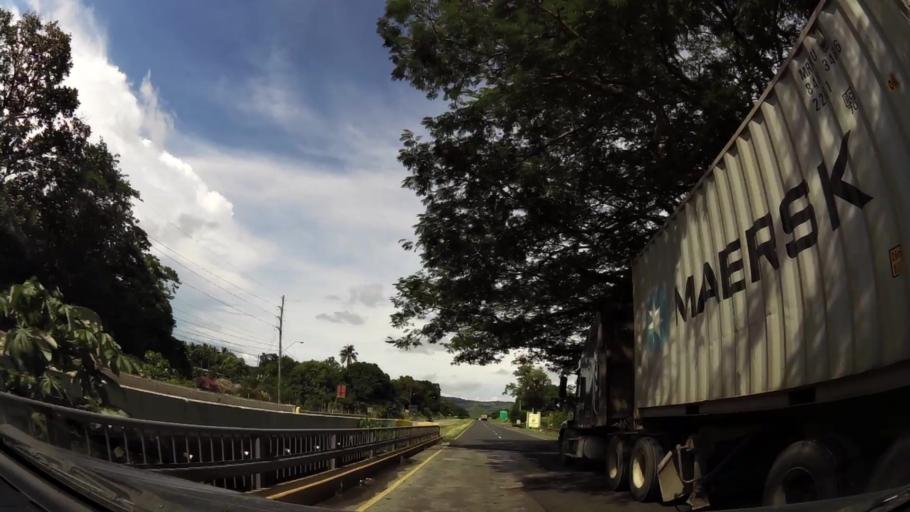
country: PA
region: Panama
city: Capira
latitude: 8.6886
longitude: -79.8689
